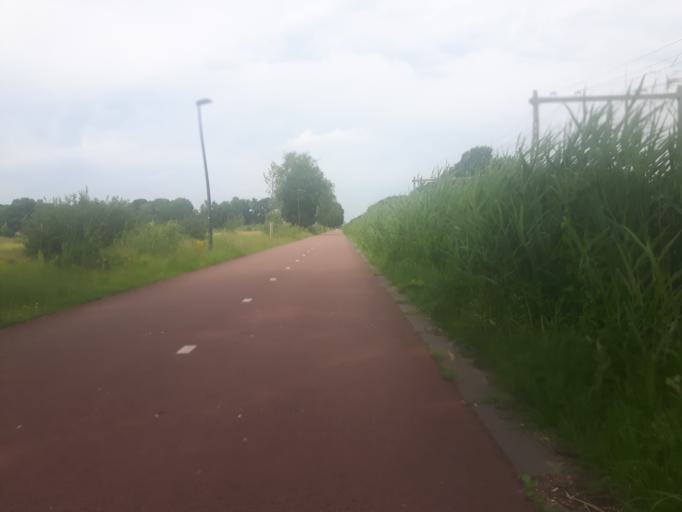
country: NL
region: Overijssel
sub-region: Gemeente Hengelo
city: Hengelo
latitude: 52.2461
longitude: 6.8246
